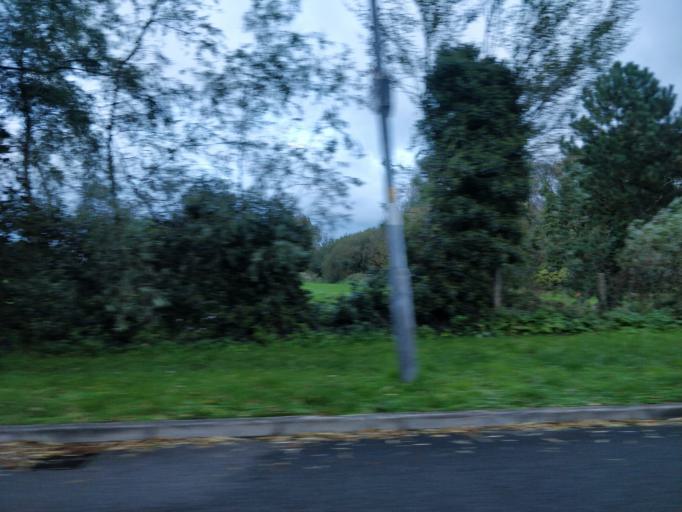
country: GB
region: England
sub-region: Sefton
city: Southport
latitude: 53.6618
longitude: -2.9861
